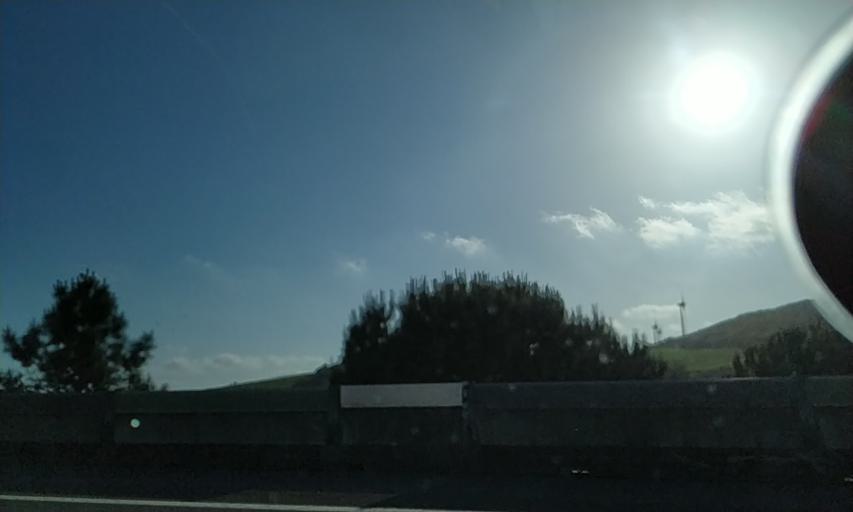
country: PT
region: Lisbon
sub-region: Torres Vedras
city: Torres Vedras
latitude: 39.0617
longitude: -9.2398
